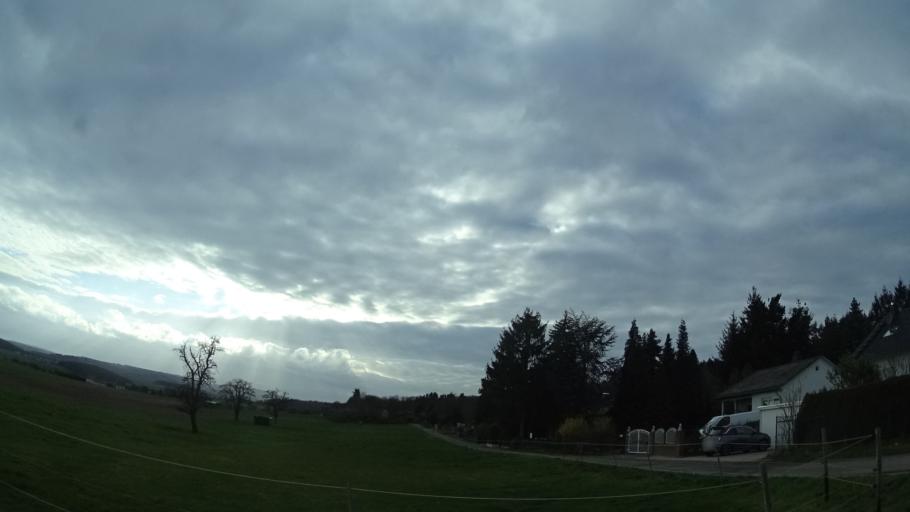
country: DE
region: Rheinland-Pfalz
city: Waldalgesheim
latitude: 49.9660
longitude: 7.8305
